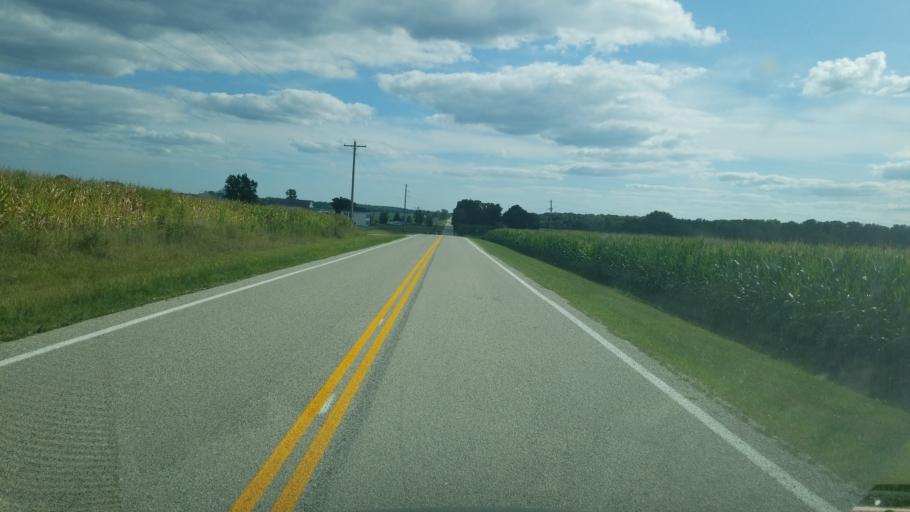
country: US
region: Ohio
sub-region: Logan County
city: De Graff
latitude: 40.2414
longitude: -83.9388
